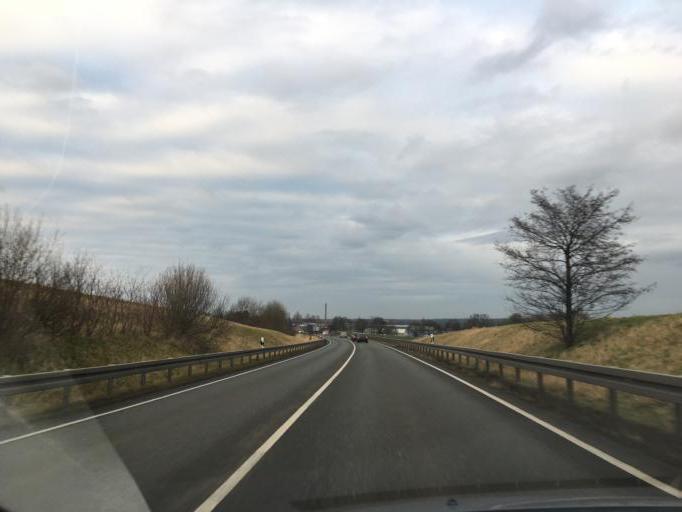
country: DE
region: Thuringia
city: Nobitz
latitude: 50.9952
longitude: 12.4703
